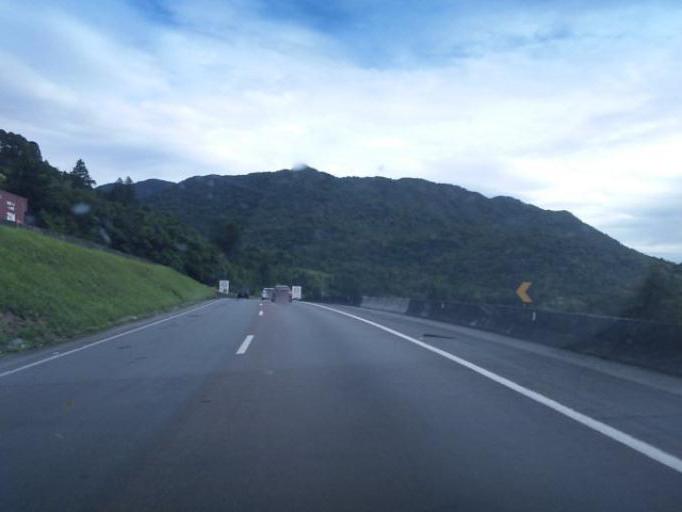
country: BR
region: Parana
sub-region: Campina Grande Do Sul
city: Campina Grande do Sul
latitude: -25.1606
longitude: -48.8622
